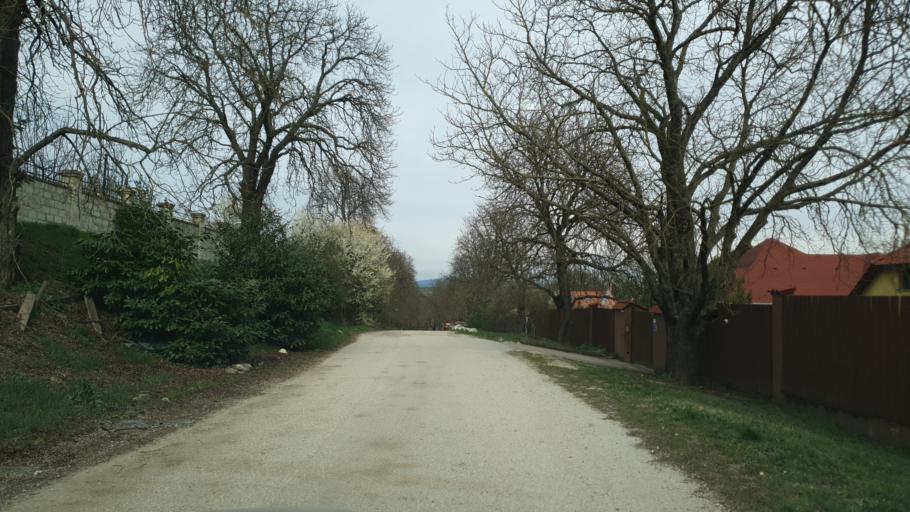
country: HU
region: Fejer
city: Etyek
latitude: 47.4542
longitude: 18.7229
